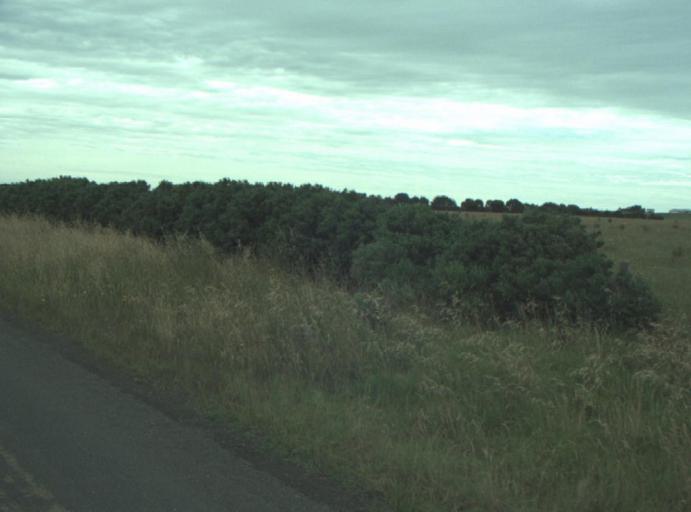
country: AU
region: Victoria
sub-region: Greater Geelong
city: Clifton Springs
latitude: -38.1923
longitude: 144.6080
